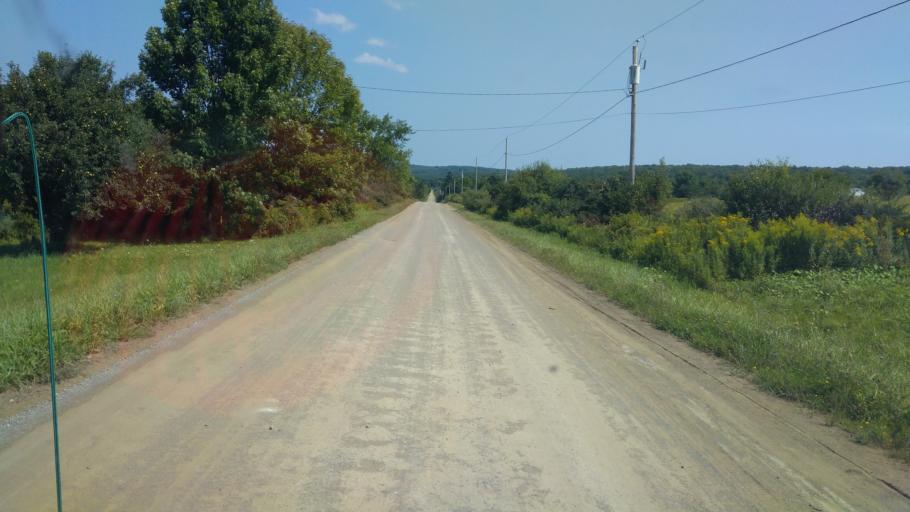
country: US
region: New York
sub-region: Allegany County
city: Houghton
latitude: 42.3503
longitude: -78.0623
